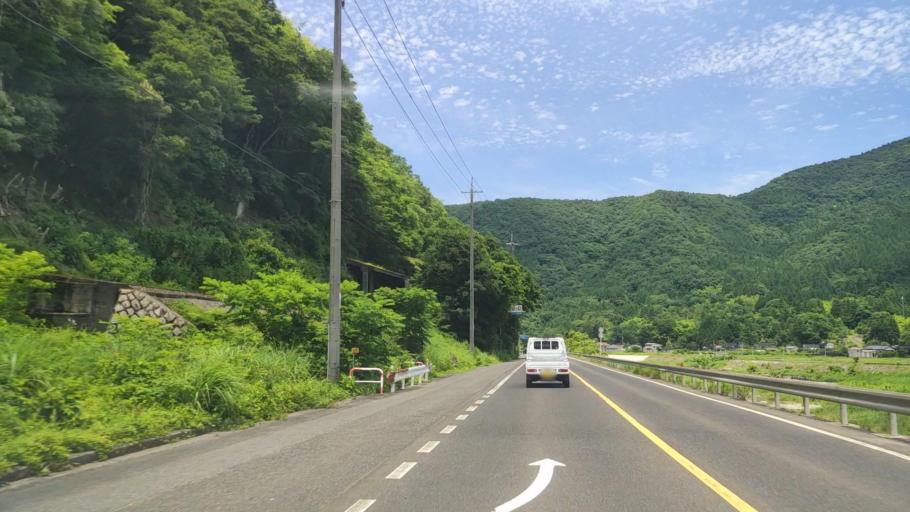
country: JP
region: Tottori
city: Tottori
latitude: 35.3630
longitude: 134.3781
